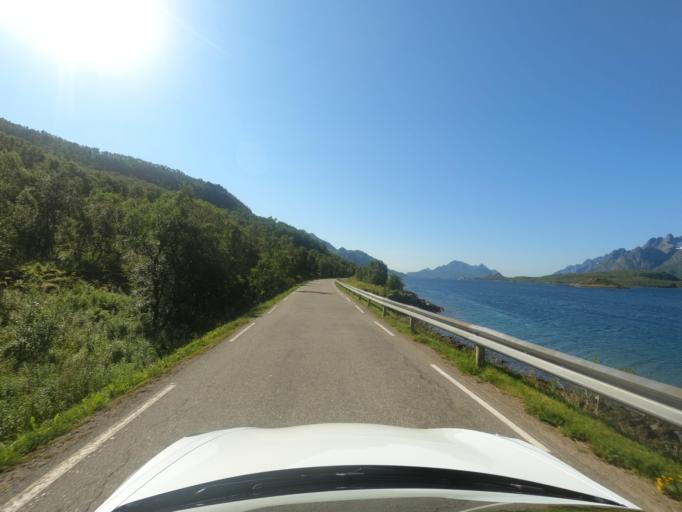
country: NO
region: Nordland
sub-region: Hadsel
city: Stokmarknes
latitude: 68.3731
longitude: 15.0766
